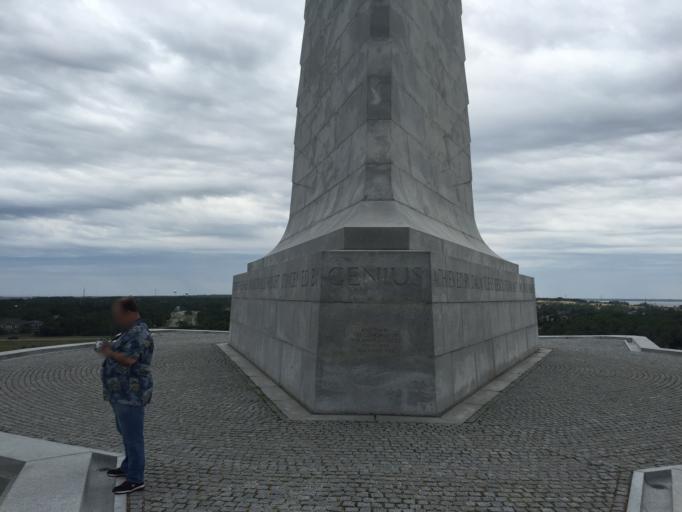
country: US
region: North Carolina
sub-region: Dare County
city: Kill Devil Hills
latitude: 36.0145
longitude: -75.6679
